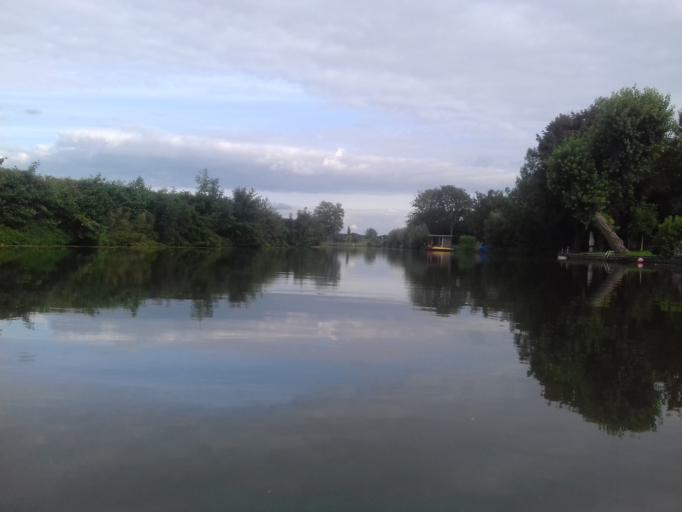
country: NL
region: Gelderland
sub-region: Gemeente Culemborg
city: Culemborg
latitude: 51.8790
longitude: 5.1899
